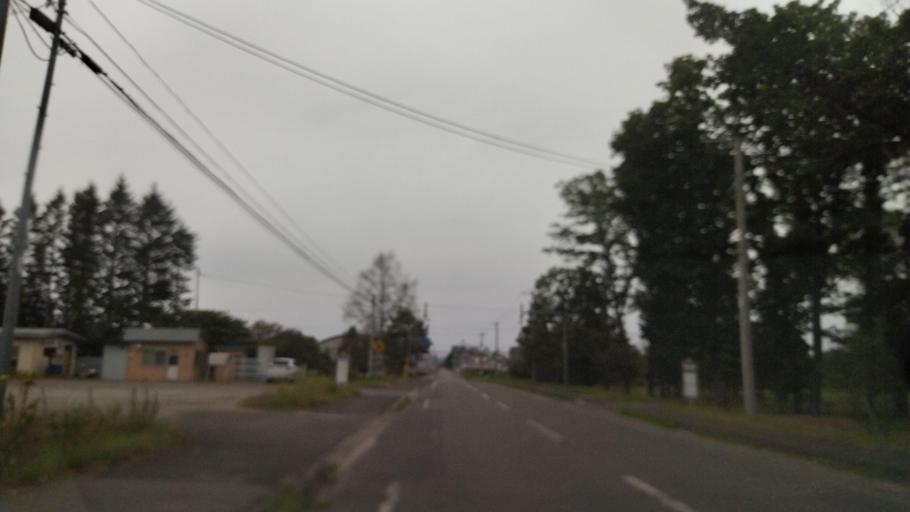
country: JP
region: Hokkaido
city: Otofuke
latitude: 43.2284
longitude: 143.2801
